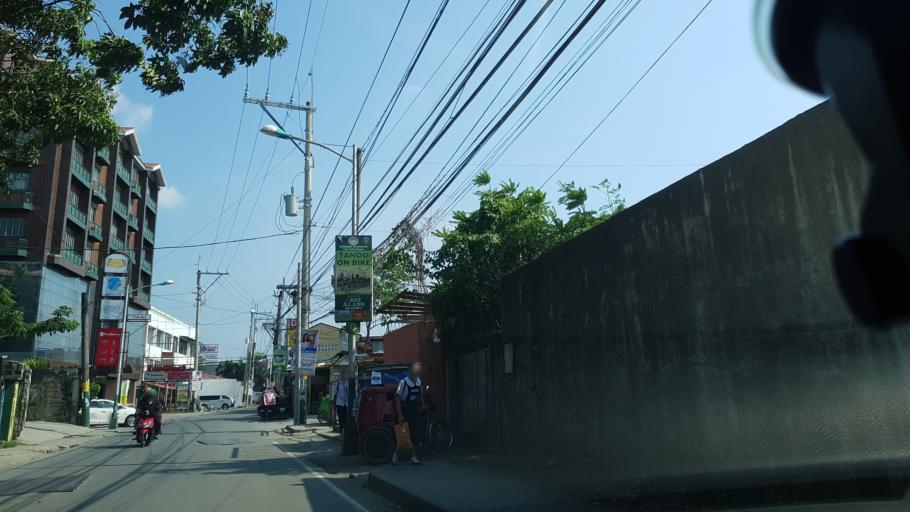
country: PH
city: Sambayanihan People's Village
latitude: 14.4955
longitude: 121.0139
